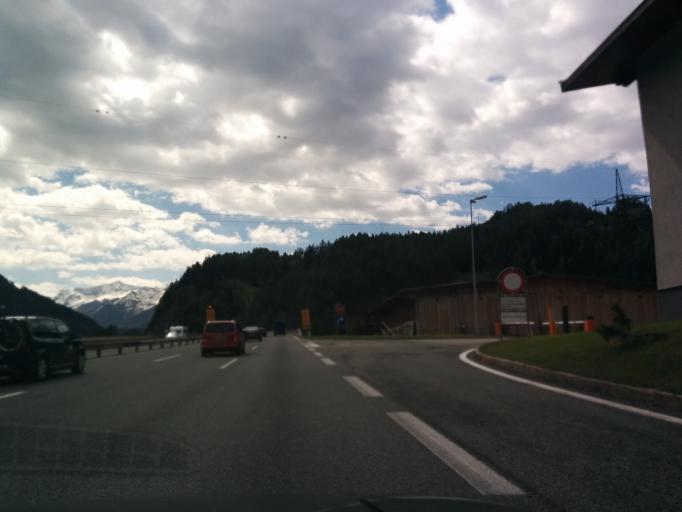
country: AT
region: Tyrol
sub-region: Politischer Bezirk Innsbruck Land
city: Steinach am Brenner
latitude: 47.0796
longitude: 11.4704
